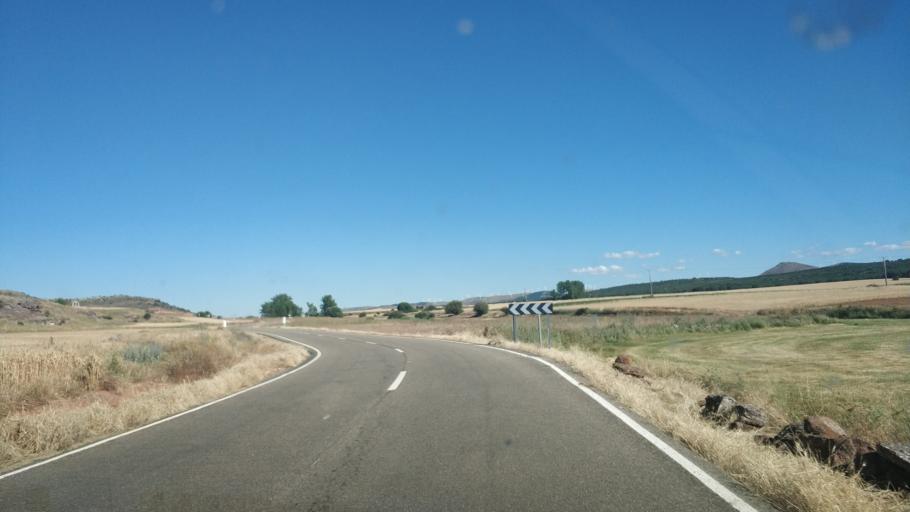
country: ES
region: Castille and Leon
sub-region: Provincia de Soria
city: Montejo de Tiermes
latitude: 41.3646
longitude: -3.1902
